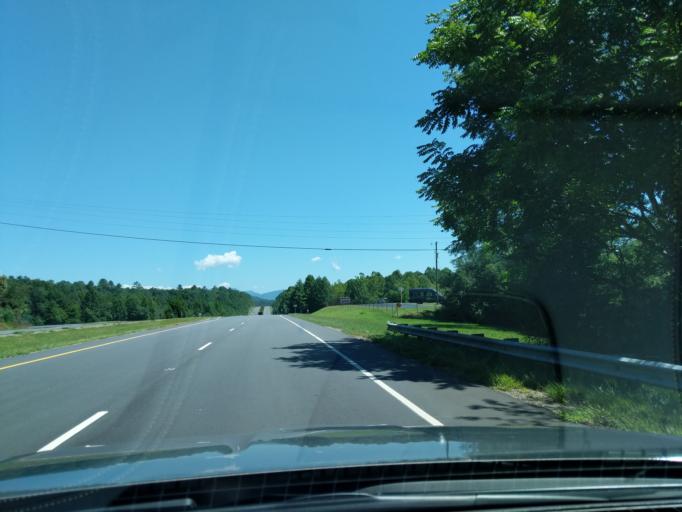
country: US
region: North Carolina
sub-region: Macon County
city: Franklin
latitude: 35.1574
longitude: -83.4582
